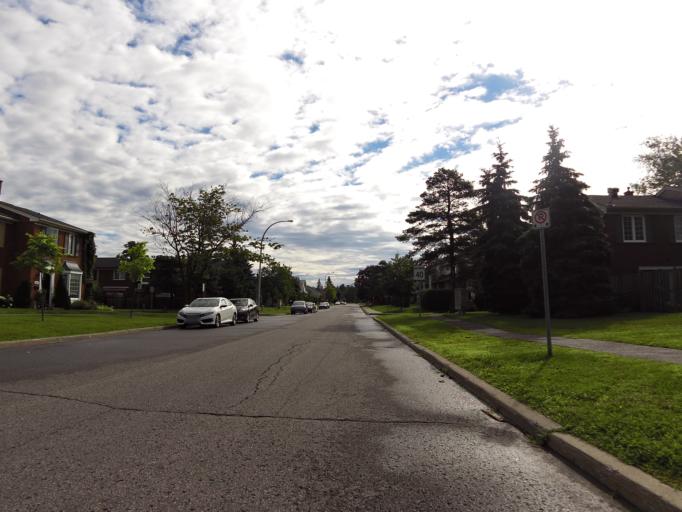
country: CA
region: Ontario
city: Bells Corners
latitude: 45.3368
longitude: -75.7949
